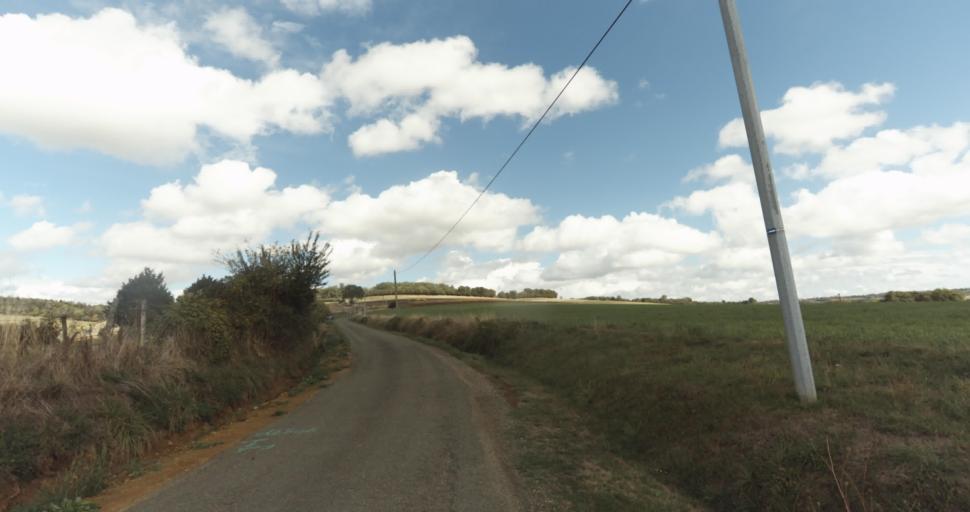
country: FR
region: Lower Normandy
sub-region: Departement de l'Orne
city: Gace
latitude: 48.7738
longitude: 0.3102
